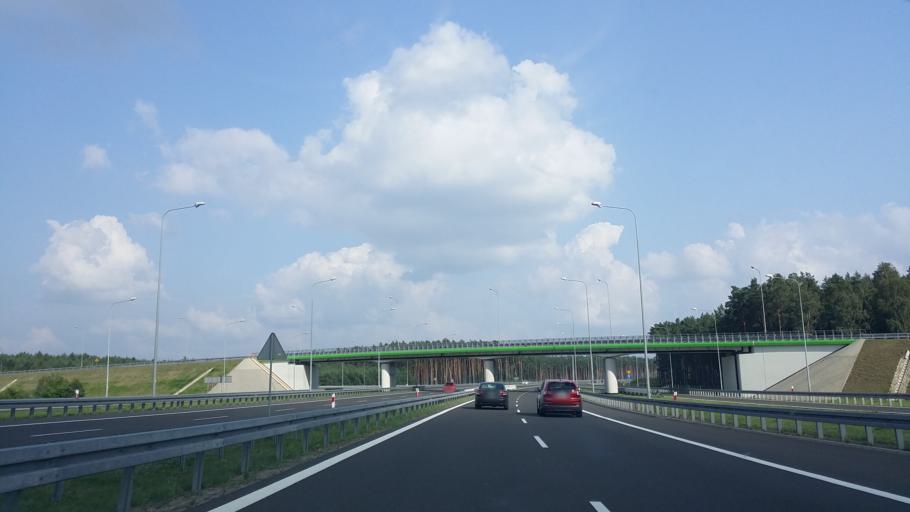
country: PL
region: Lubusz
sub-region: Powiat miedzyrzecki
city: Skwierzyna
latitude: 52.5601
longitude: 15.5265
